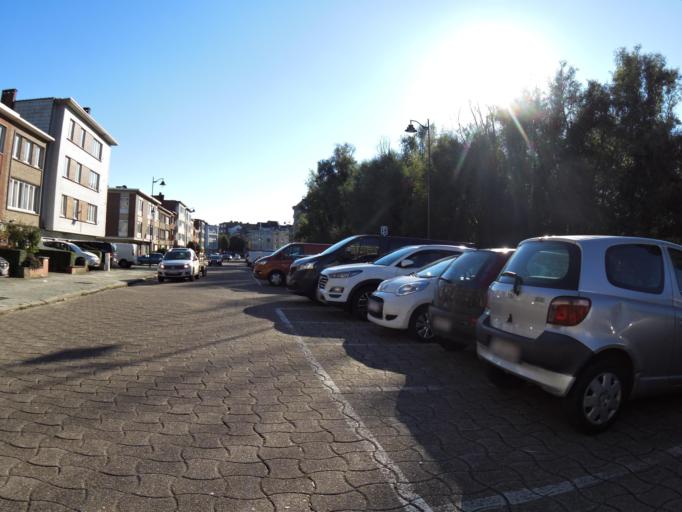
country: BE
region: Brussels Capital
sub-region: Bruxelles-Capitale
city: Brussels
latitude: 50.8503
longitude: 4.3045
